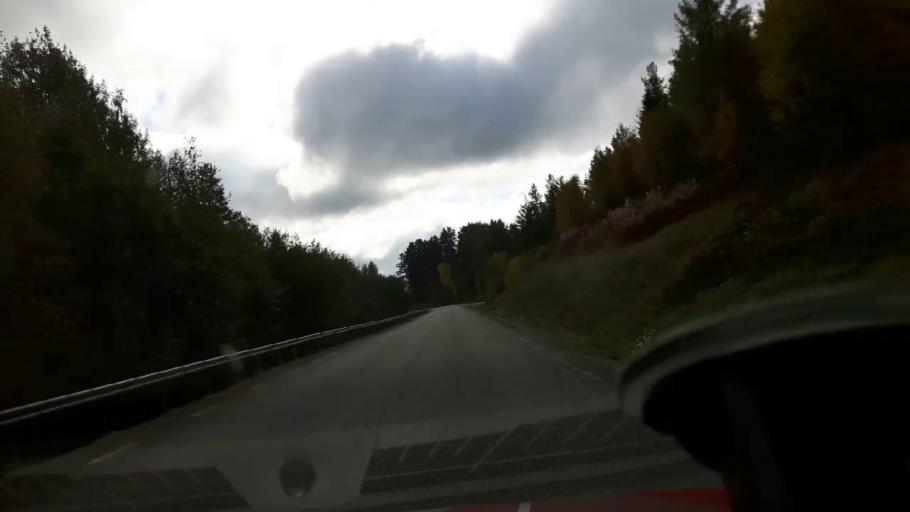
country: SE
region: Gaevleborg
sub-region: Ljusdals Kommun
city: Farila
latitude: 61.7945
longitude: 15.9134
